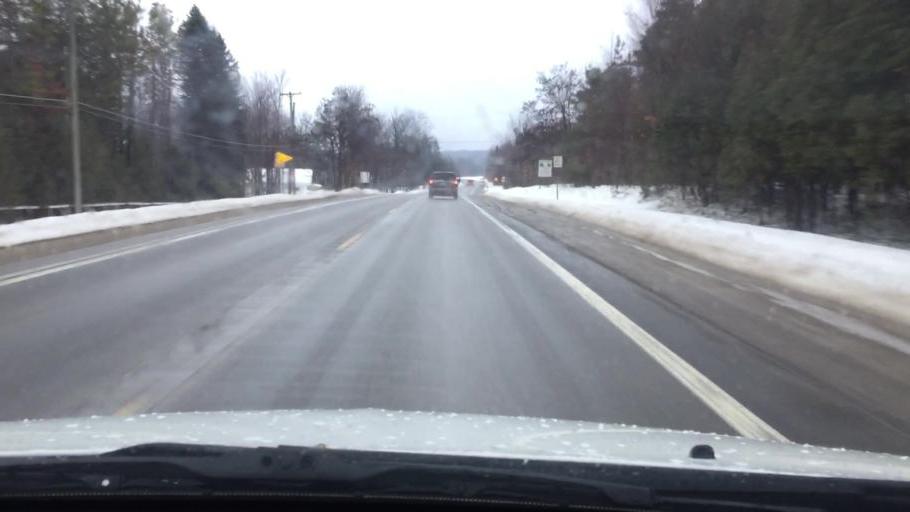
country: US
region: Michigan
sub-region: Charlevoix County
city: East Jordan
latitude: 45.1909
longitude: -85.1646
